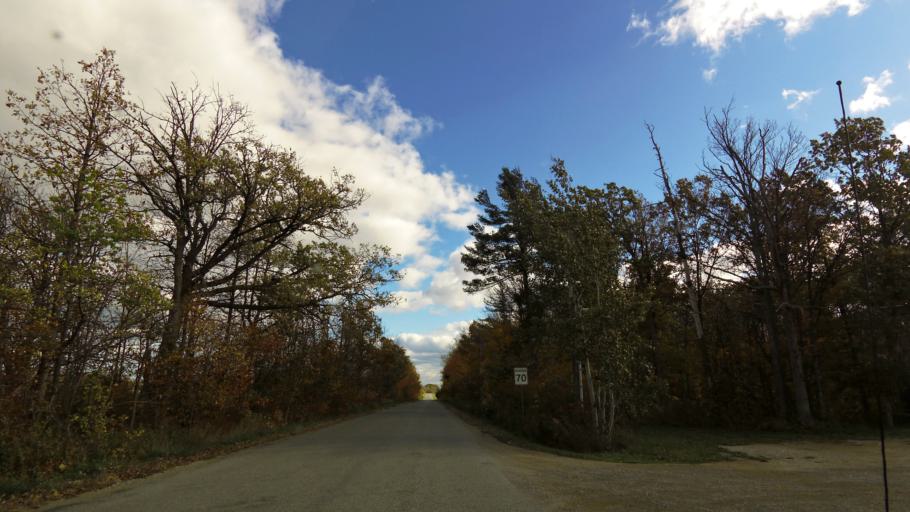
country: CA
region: Ontario
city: Burlington
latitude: 43.4458
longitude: -79.8506
